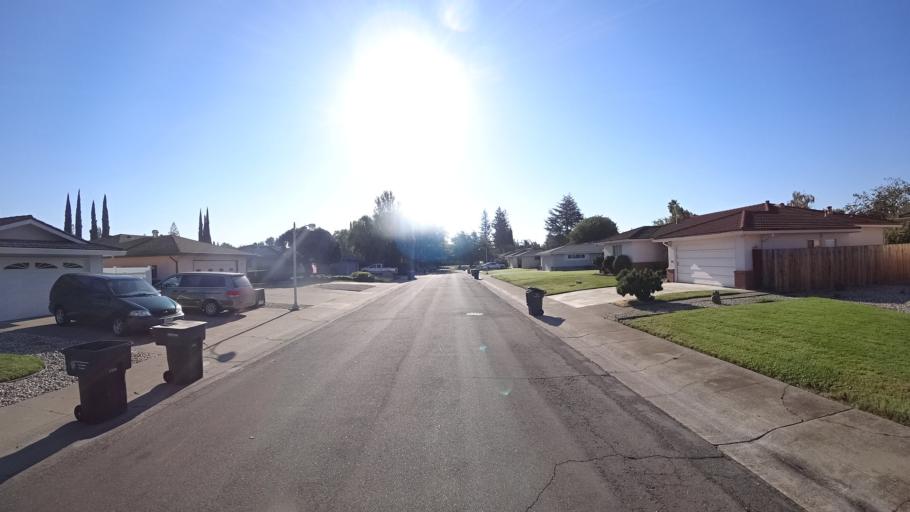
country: US
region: California
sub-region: Yolo County
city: West Sacramento
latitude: 38.5049
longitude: -121.5486
